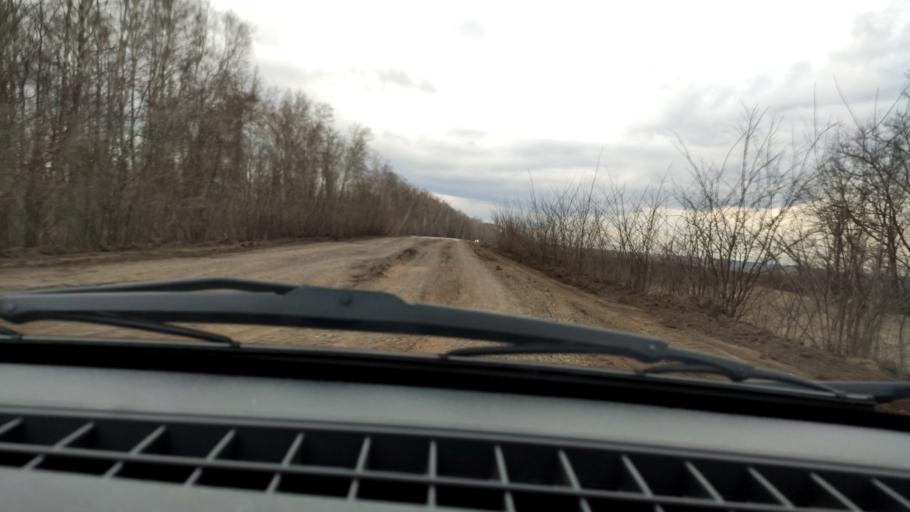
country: RU
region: Bashkortostan
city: Semiletka
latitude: 55.2647
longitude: 54.6336
